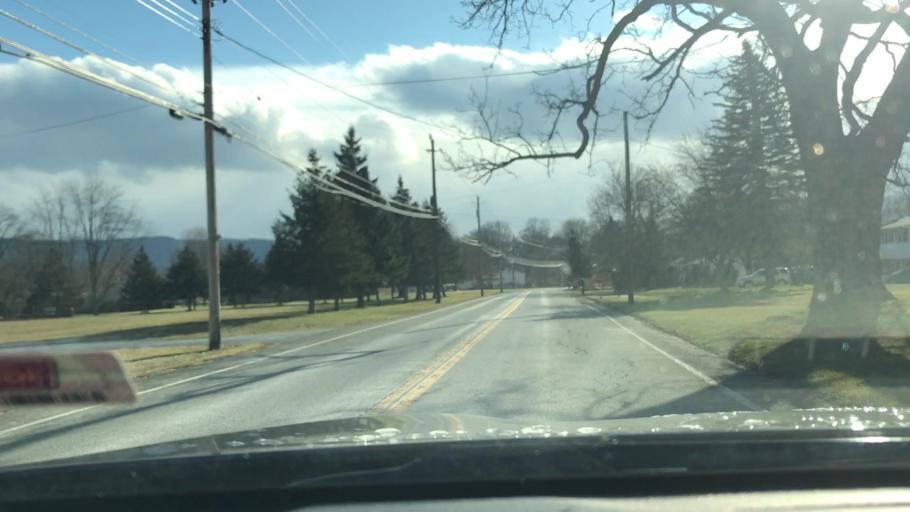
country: US
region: New York
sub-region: Chemung County
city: Big Flats
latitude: 42.1589
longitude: -76.9240
